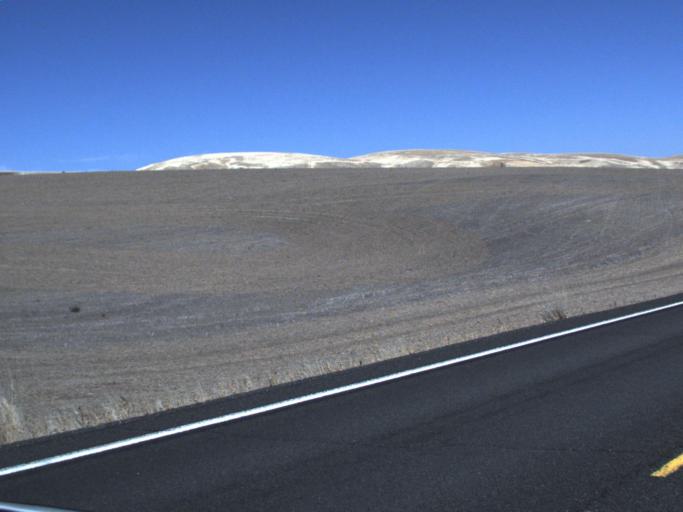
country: US
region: Washington
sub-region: Walla Walla County
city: Garrett
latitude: 46.2900
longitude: -118.5421
